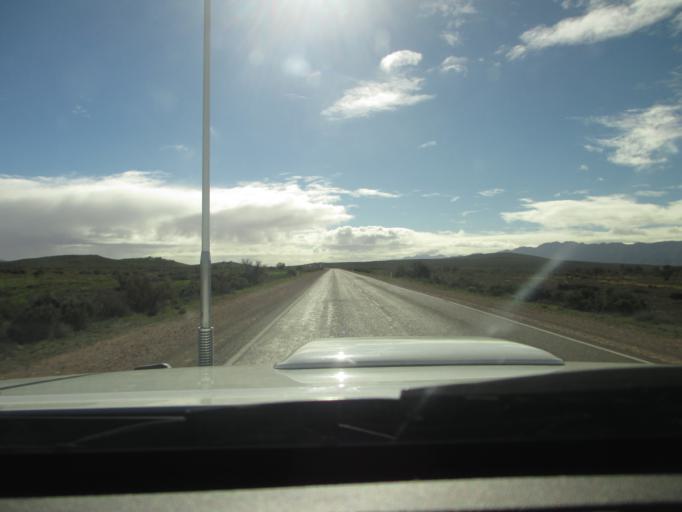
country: AU
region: South Australia
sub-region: Flinders Ranges
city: Quorn
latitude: -31.7543
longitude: 138.3341
